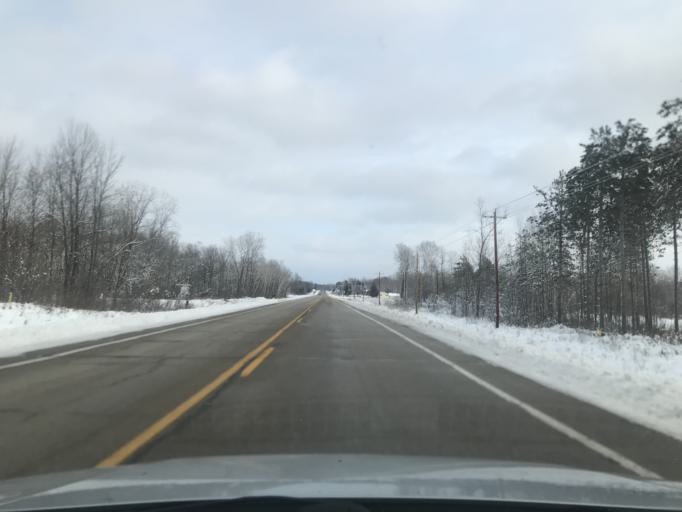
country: US
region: Wisconsin
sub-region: Oconto County
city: Oconto Falls
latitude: 44.8867
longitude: -88.0342
